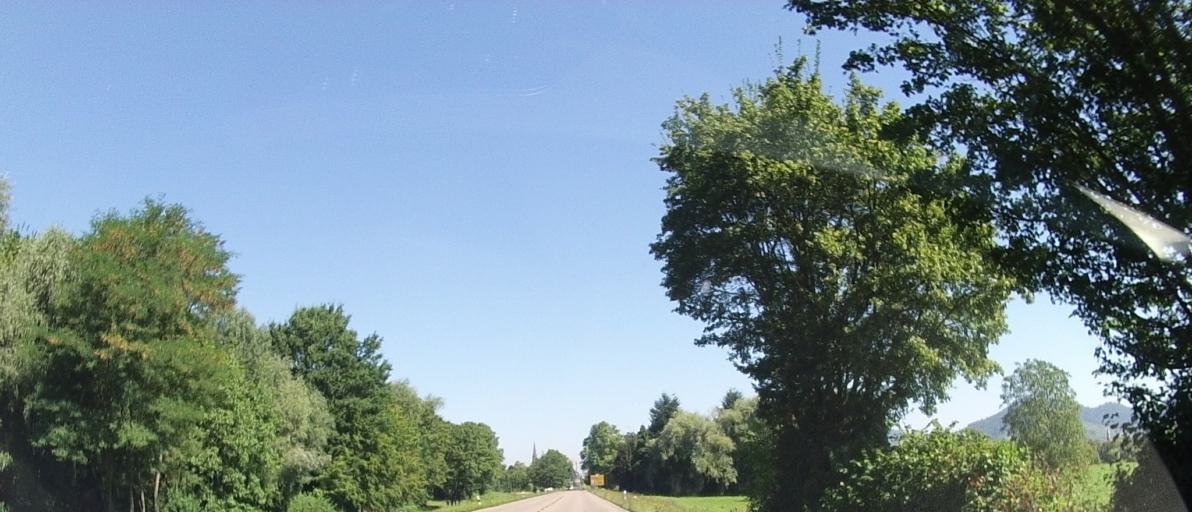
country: DE
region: Baden-Wuerttemberg
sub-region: Karlsruhe Region
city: Buhl
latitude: 48.6863
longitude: 8.1296
